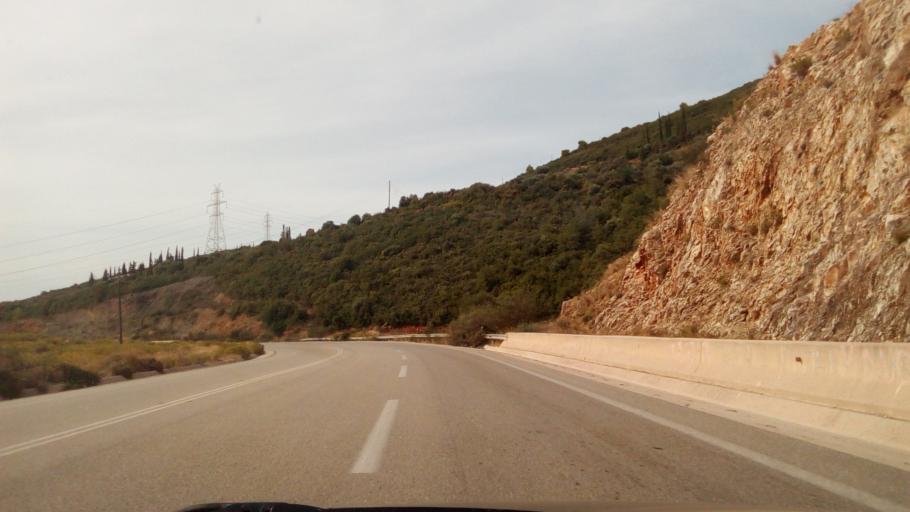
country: GR
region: West Greece
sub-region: Nomos Aitolias kai Akarnanias
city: Nafpaktos
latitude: 38.4067
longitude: 21.8375
